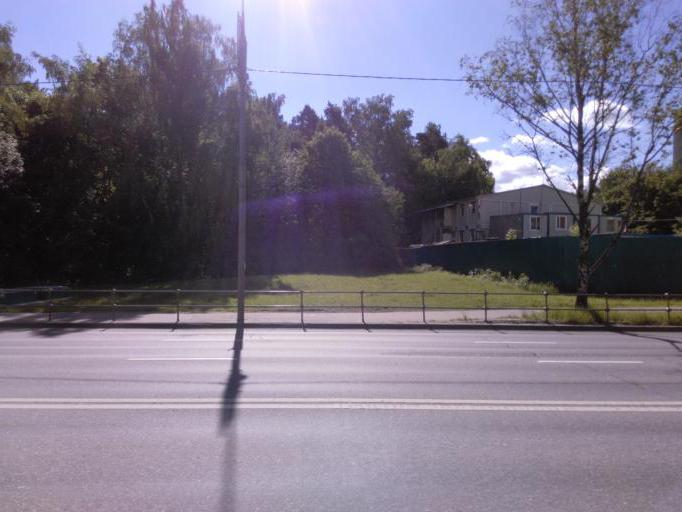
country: RU
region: Moscow
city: Zelenograd
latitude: 55.9864
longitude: 37.1816
